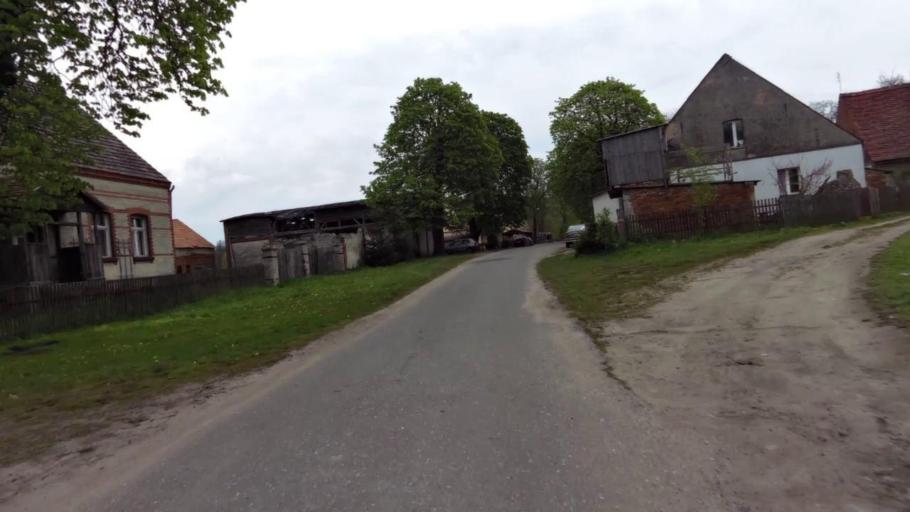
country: PL
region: West Pomeranian Voivodeship
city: Trzcinsko Zdroj
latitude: 52.9462
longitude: 14.7234
